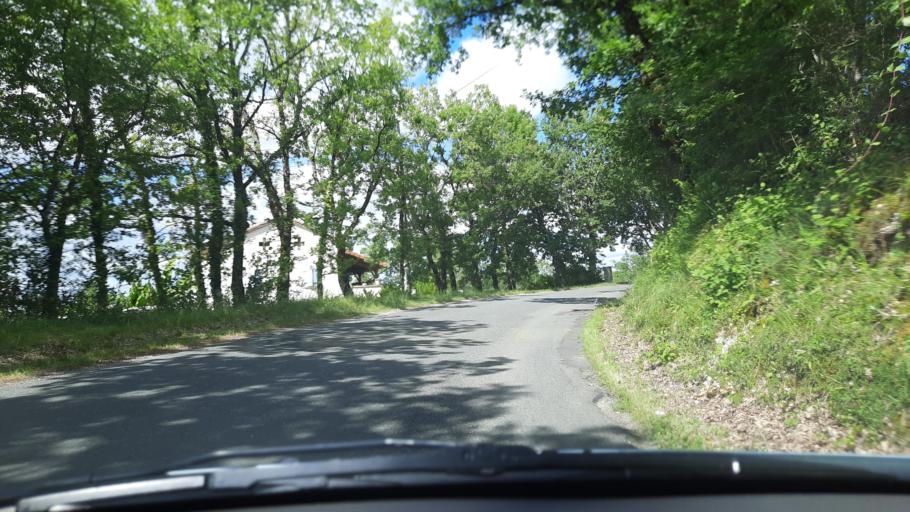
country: FR
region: Midi-Pyrenees
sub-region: Departement du Lot
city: Castelnau-Montratier
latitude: 44.2946
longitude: 1.4549
